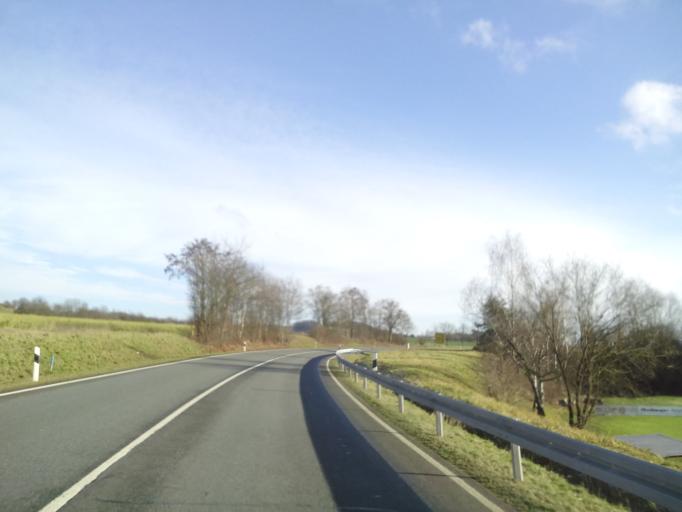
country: DE
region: Bavaria
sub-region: Upper Franconia
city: Mainleus
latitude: 50.1144
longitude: 11.3484
